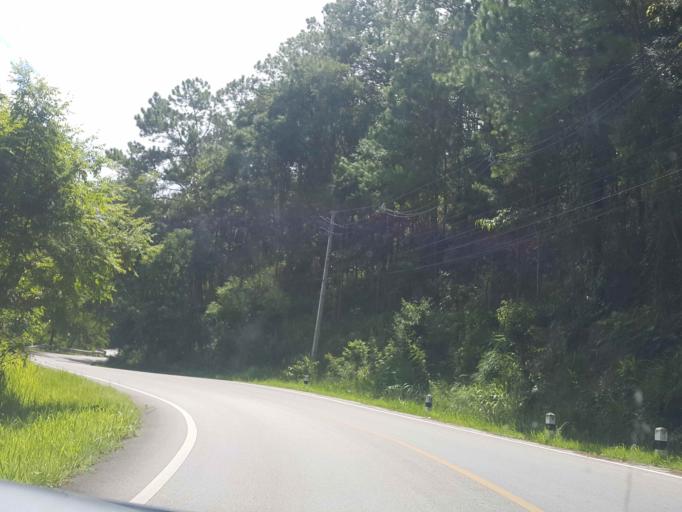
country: TH
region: Chiang Mai
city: Samoeng
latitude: 18.8747
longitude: 98.7812
